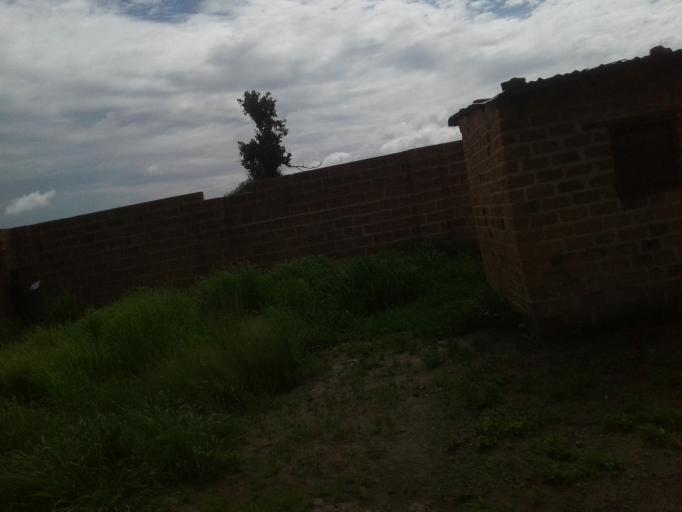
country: CD
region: Katanga
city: Lubumbashi
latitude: -11.4657
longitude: 27.5466
